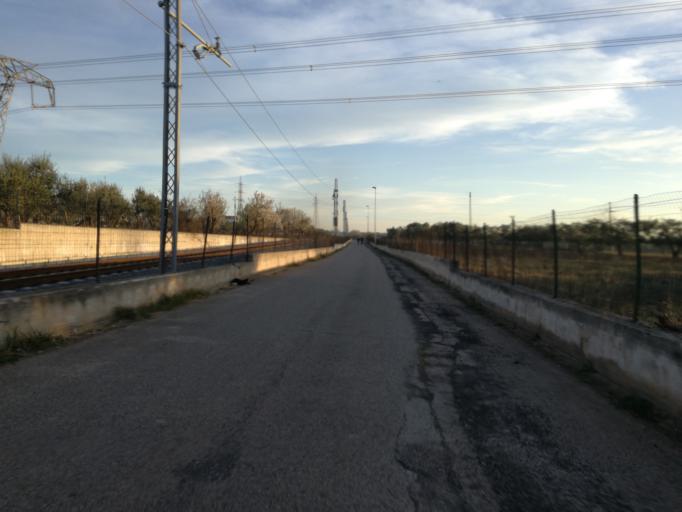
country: IT
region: Apulia
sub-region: Provincia di Bari
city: Lamie
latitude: 41.0300
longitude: 16.8775
